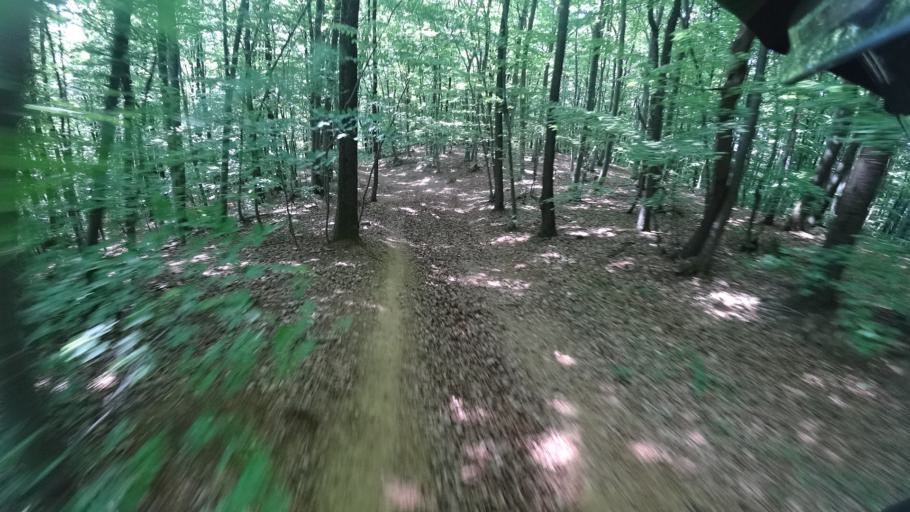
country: HR
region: Grad Zagreb
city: Kasina
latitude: 45.9448
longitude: 15.9593
